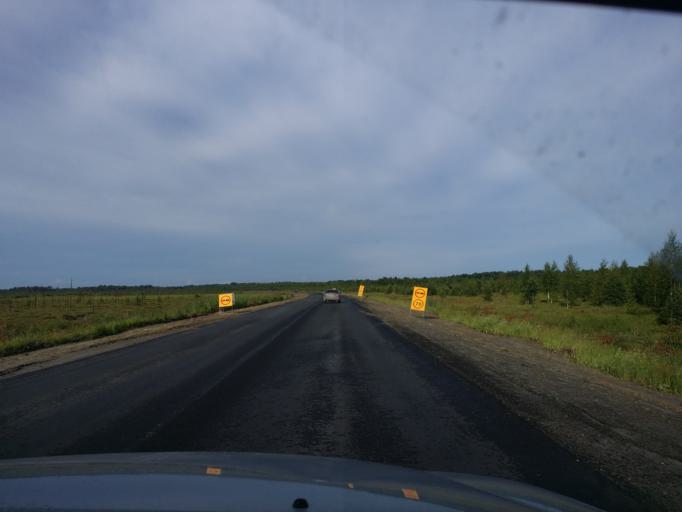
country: RU
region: Tjumen
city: Uvat
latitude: 59.3648
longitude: 68.9943
